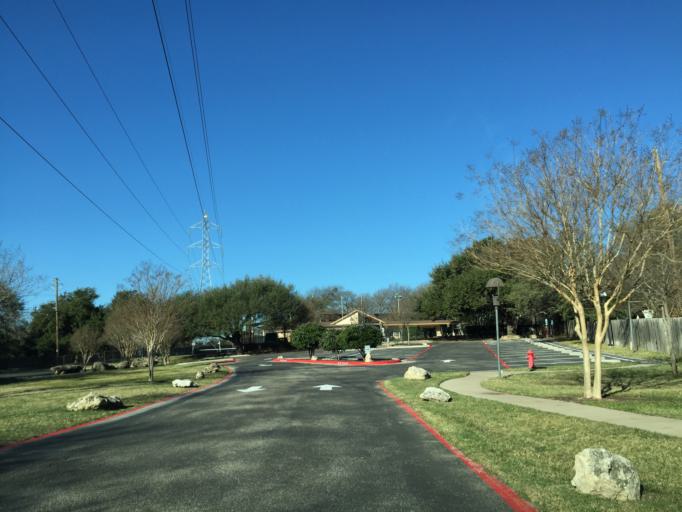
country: US
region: Texas
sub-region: Williamson County
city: Jollyville
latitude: 30.4046
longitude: -97.7375
